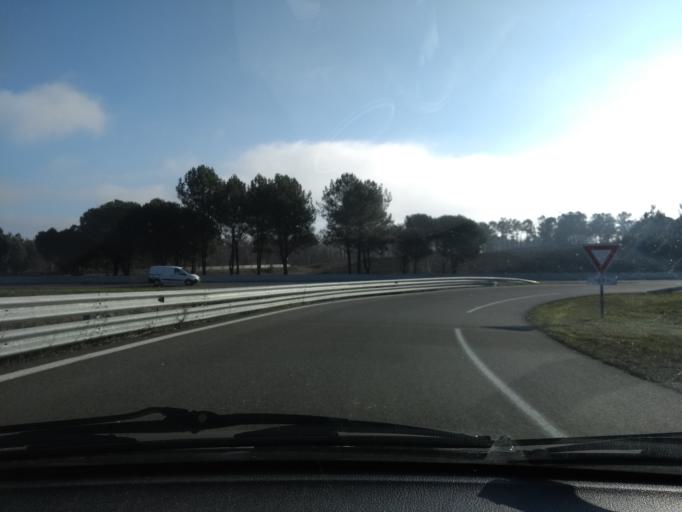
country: FR
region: Aquitaine
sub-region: Departement de la Gironde
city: Biganos
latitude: 44.6266
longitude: -0.9569
